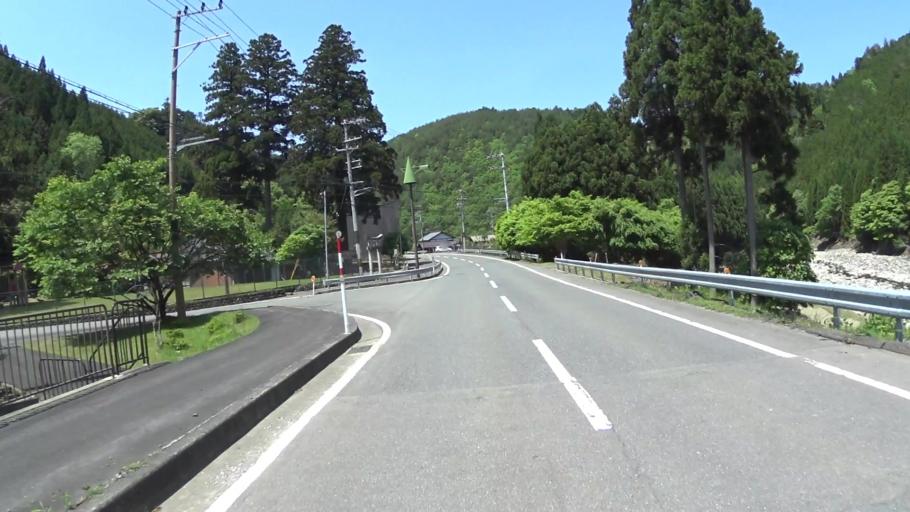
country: JP
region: Kyoto
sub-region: Kyoto-shi
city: Kamigyo-ku
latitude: 35.2079
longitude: 135.7392
